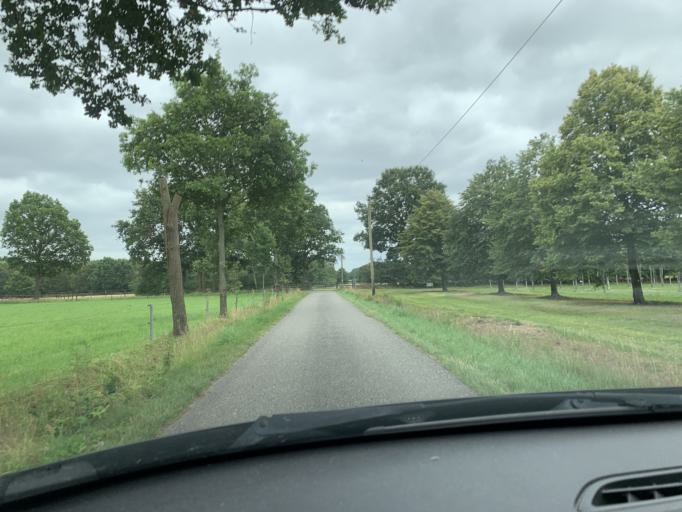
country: DE
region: Lower Saxony
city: Bad Zwischenahn
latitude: 53.2273
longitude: 7.9720
